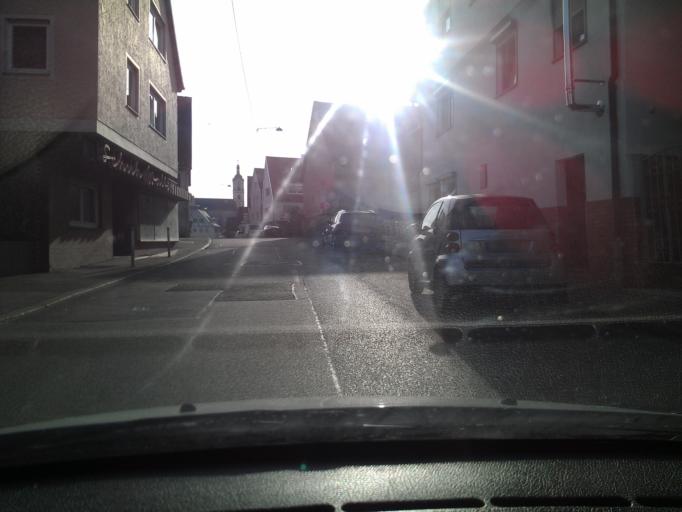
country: DE
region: Baden-Wuerttemberg
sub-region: Regierungsbezirk Stuttgart
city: Neuhausen auf den Fildern
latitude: 48.6859
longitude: 9.2783
